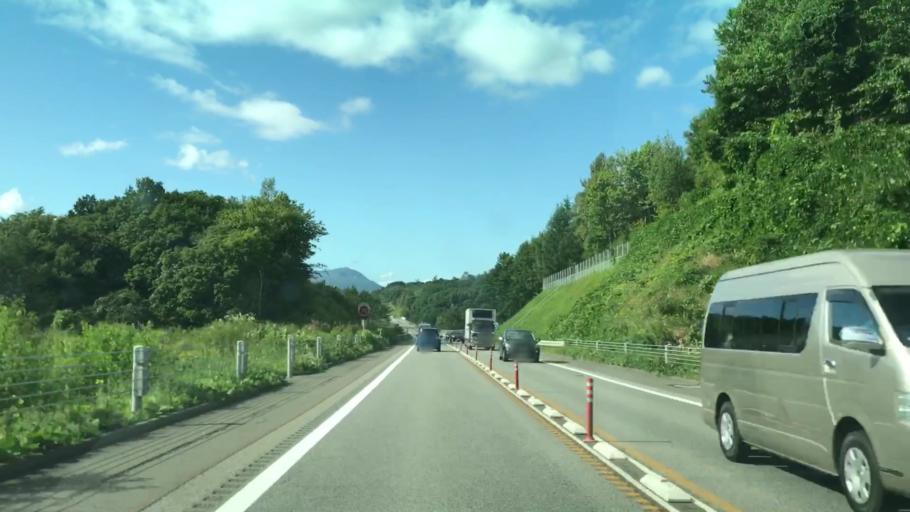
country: JP
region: Hokkaido
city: Date
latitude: 42.4302
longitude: 140.9253
